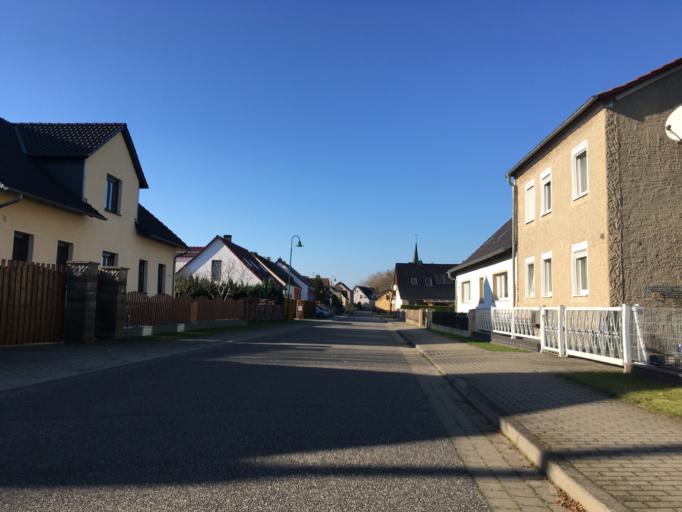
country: DE
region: Brandenburg
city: Rauen
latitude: 52.3254
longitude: 13.9537
